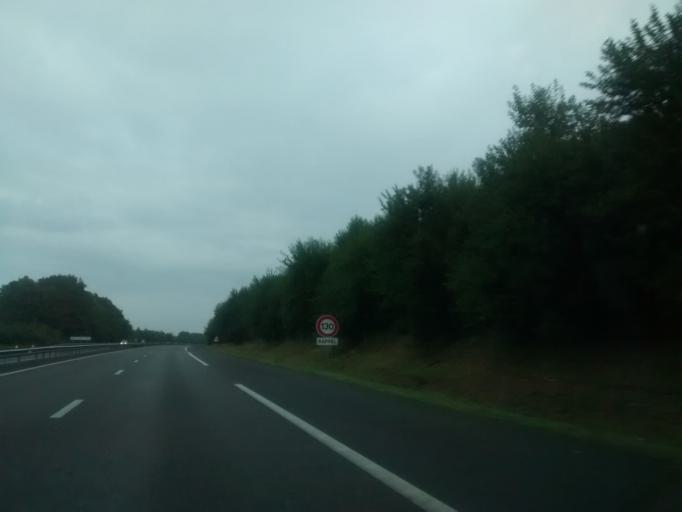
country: FR
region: Brittany
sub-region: Departement d'Ille-et-Vilaine
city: Liffre
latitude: 48.2087
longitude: -1.5230
